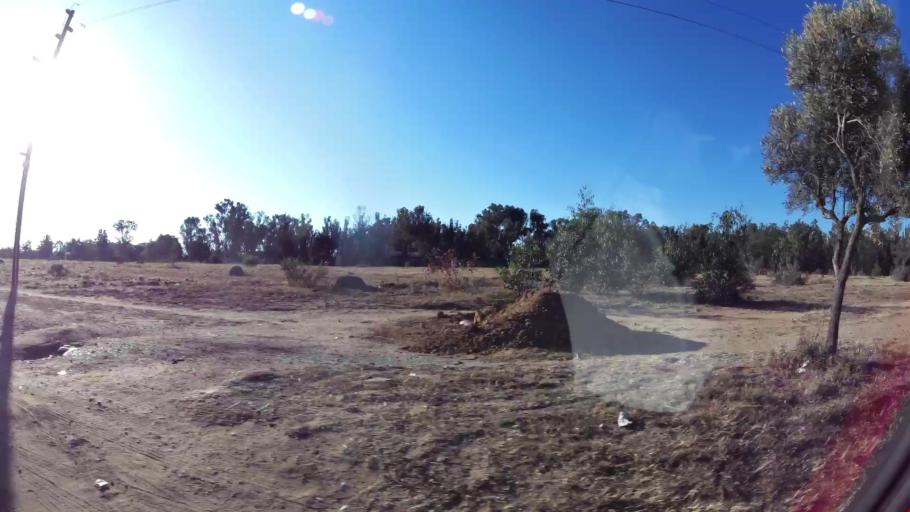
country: ZA
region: Gauteng
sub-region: City of Johannesburg Metropolitan Municipality
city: Midrand
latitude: -25.9810
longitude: 28.0894
